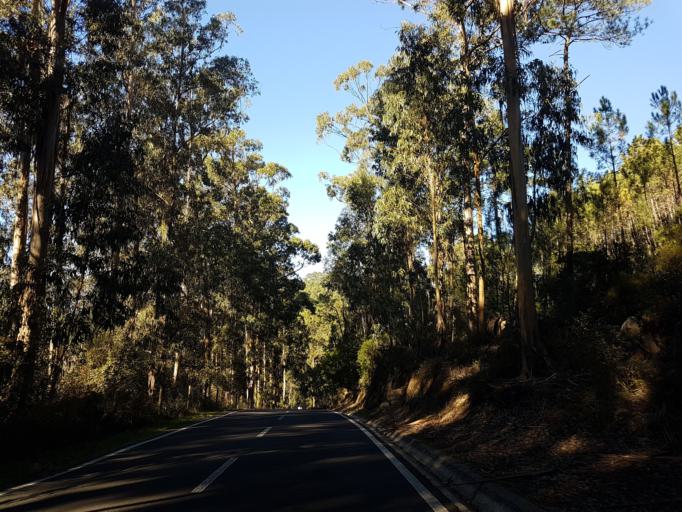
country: PT
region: Lisbon
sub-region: Cascais
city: Alcabideche
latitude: 38.7582
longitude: -9.4172
